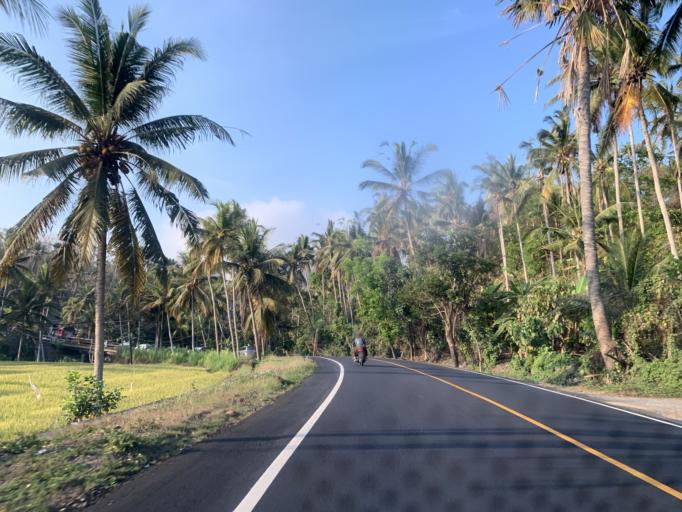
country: ID
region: Bali
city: Angkahgede
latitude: -8.4786
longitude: 114.9405
